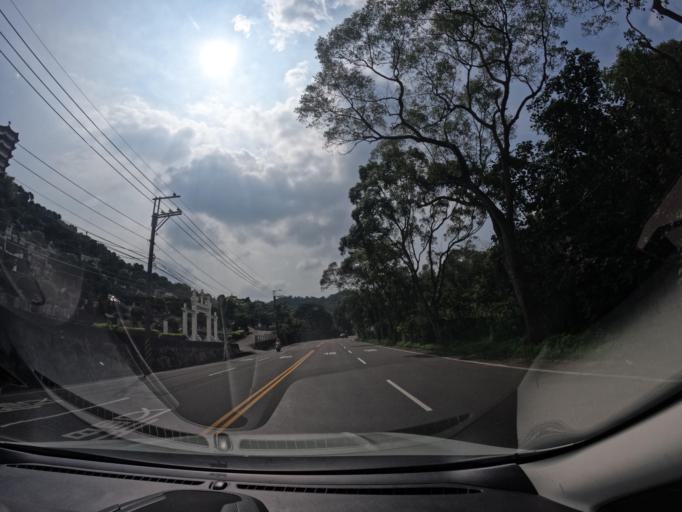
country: TW
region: Taiwan
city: Daxi
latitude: 24.9035
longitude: 121.3484
